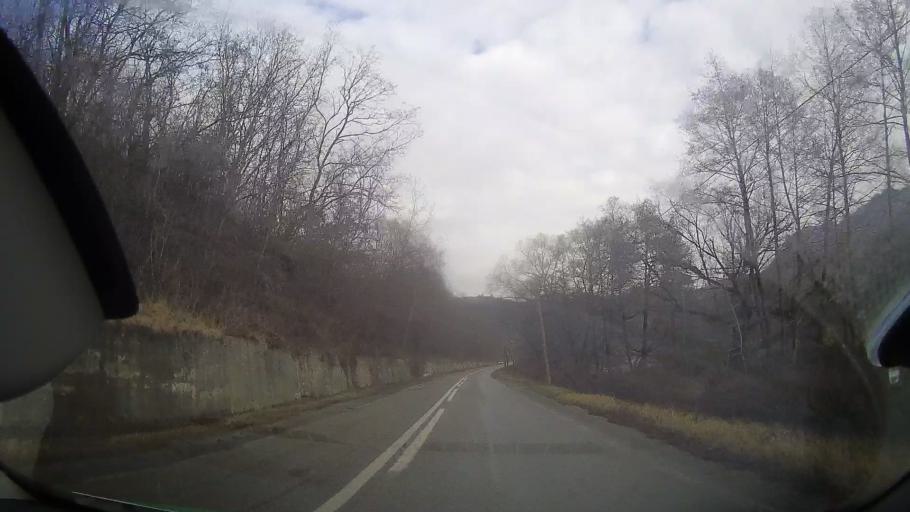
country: RO
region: Alba
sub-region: Comuna Ocolis
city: Ocolis
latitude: 46.4385
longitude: 23.4522
